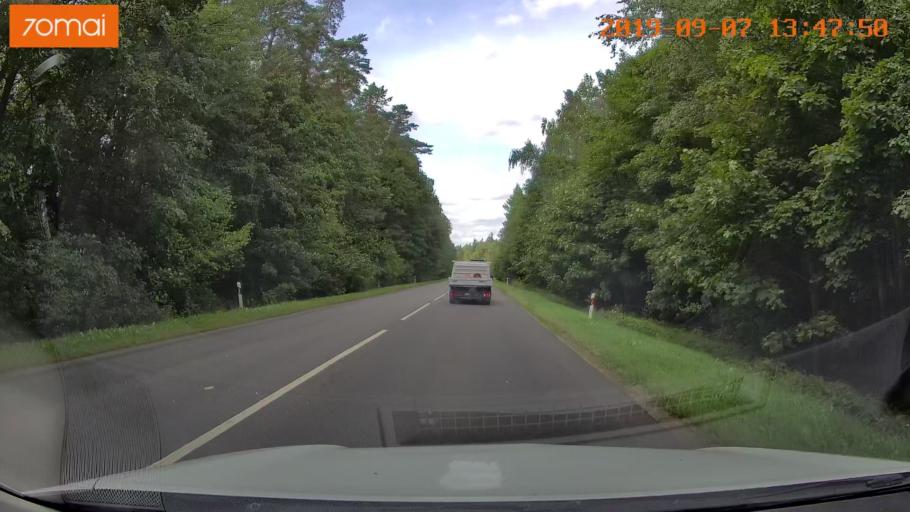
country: LT
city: Baltoji Voke
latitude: 54.5994
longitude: 25.2094
